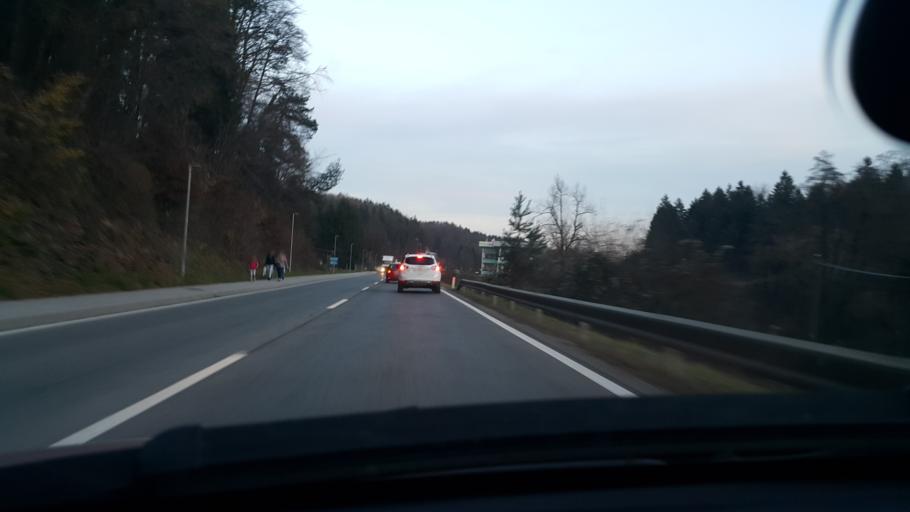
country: SI
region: Velenje
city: Velenje
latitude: 46.3537
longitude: 15.1219
